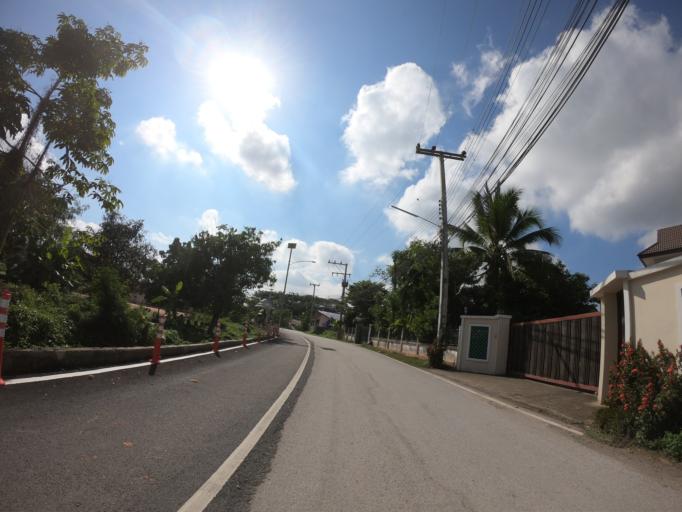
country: TH
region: Chiang Mai
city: San Sai
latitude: 18.8470
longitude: 99.0521
